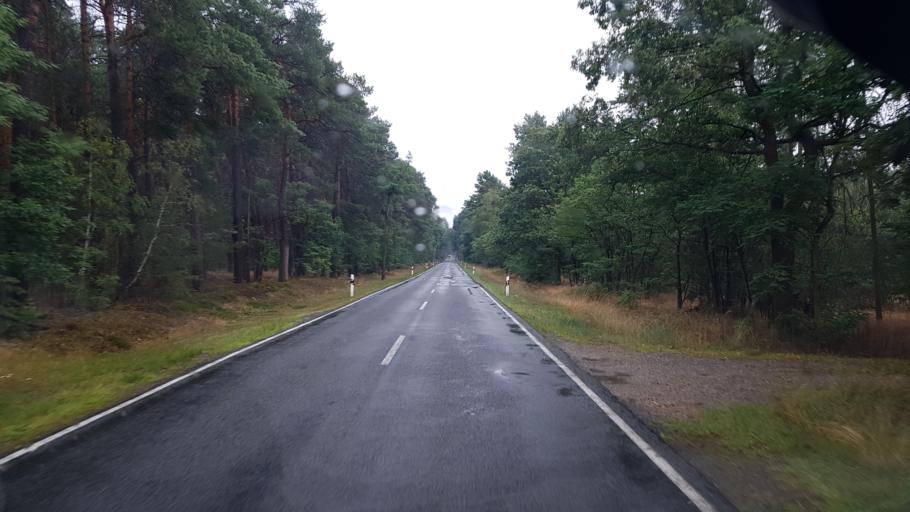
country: DE
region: Brandenburg
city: Lebusa
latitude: 51.8311
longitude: 13.4157
